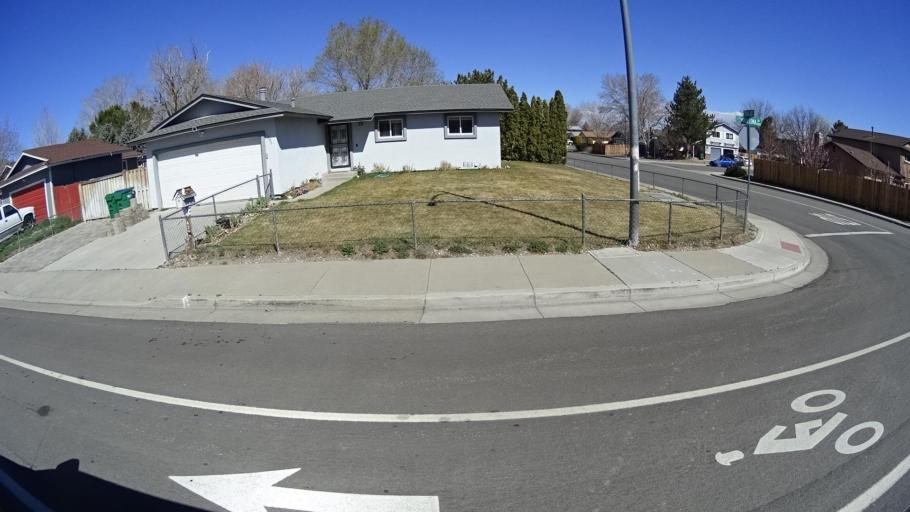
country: US
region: Nevada
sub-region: Washoe County
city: Sparks
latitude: 39.4861
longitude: -119.7501
